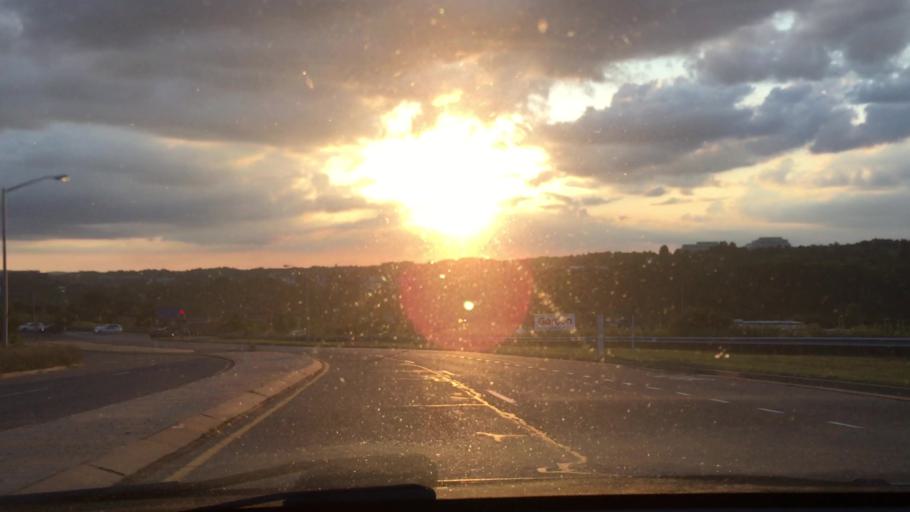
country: US
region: Pennsylvania
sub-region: Allegheny County
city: Oakdale
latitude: 40.4563
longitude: -80.1654
